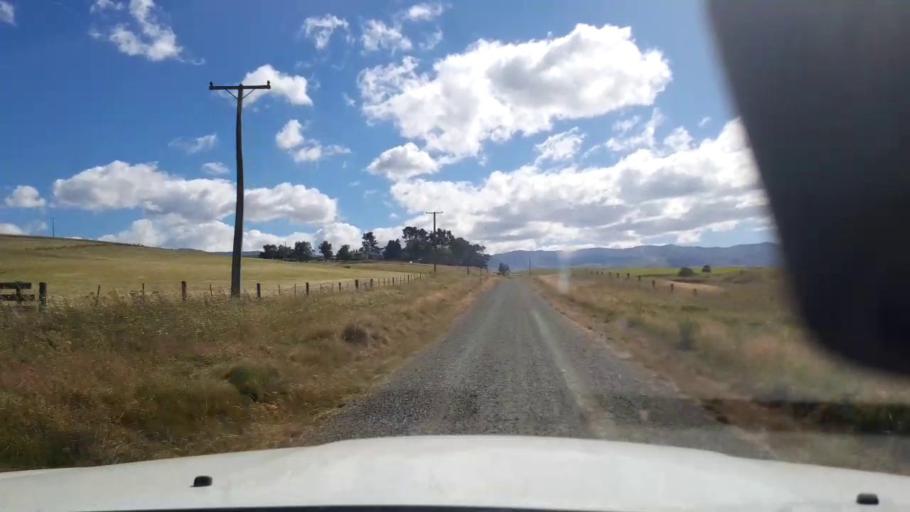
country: NZ
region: Canterbury
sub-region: Timaru District
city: Pleasant Point
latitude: -44.2396
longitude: 170.8610
